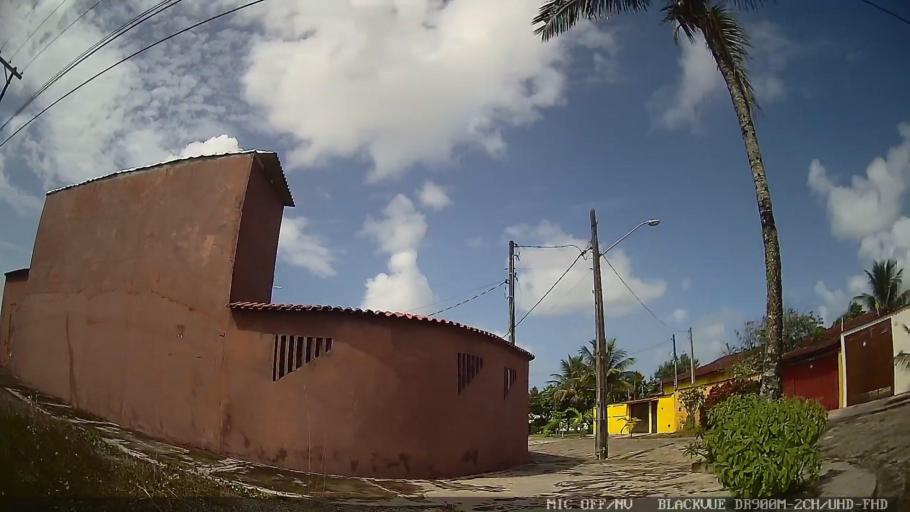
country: BR
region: Sao Paulo
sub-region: Itanhaem
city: Itanhaem
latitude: -24.1463
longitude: -46.7202
